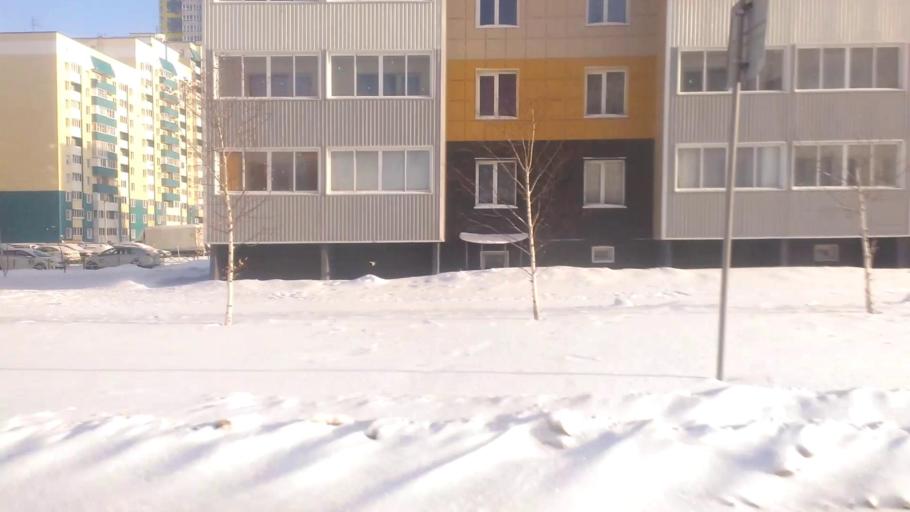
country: RU
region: Altai Krai
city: Novosilikatnyy
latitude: 53.3403
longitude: 83.6545
